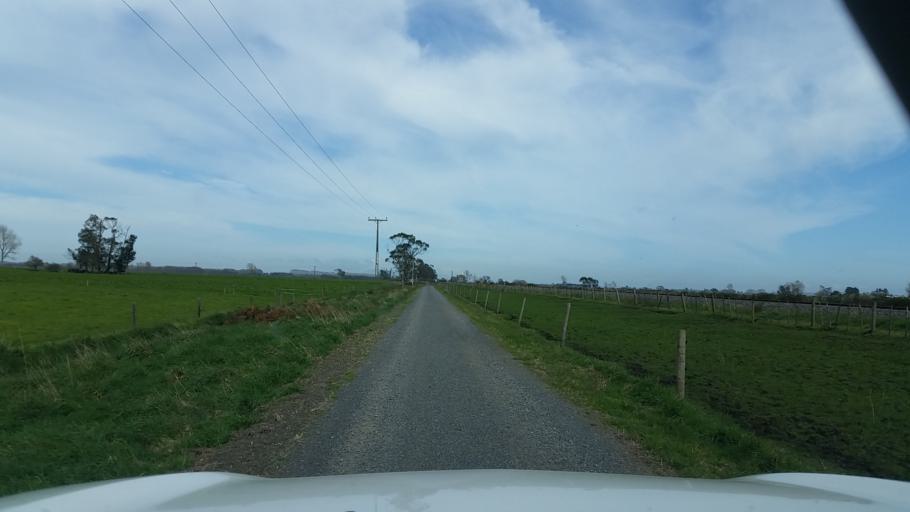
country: NZ
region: Waikato
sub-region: Waipa District
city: Cambridge
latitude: -37.6828
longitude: 175.4549
